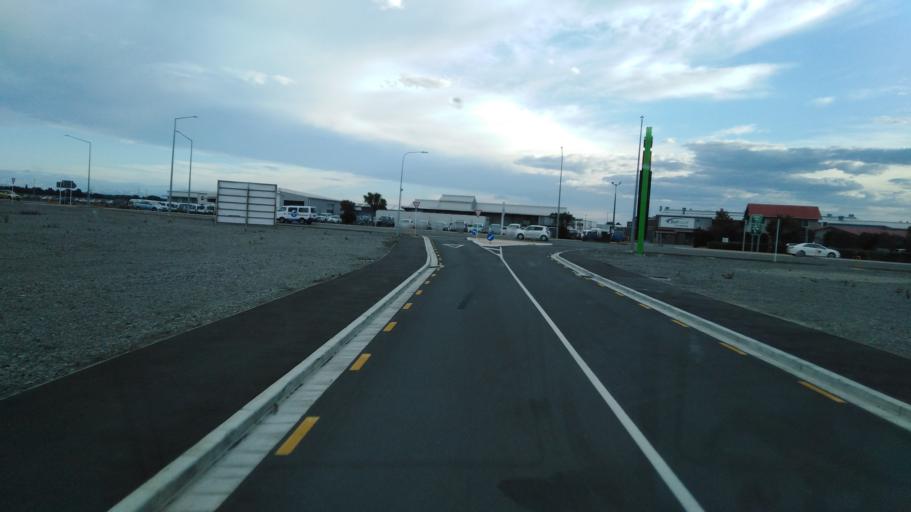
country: NZ
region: Canterbury
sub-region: Christchurch City
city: Christchurch
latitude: -43.4789
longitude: 172.5540
